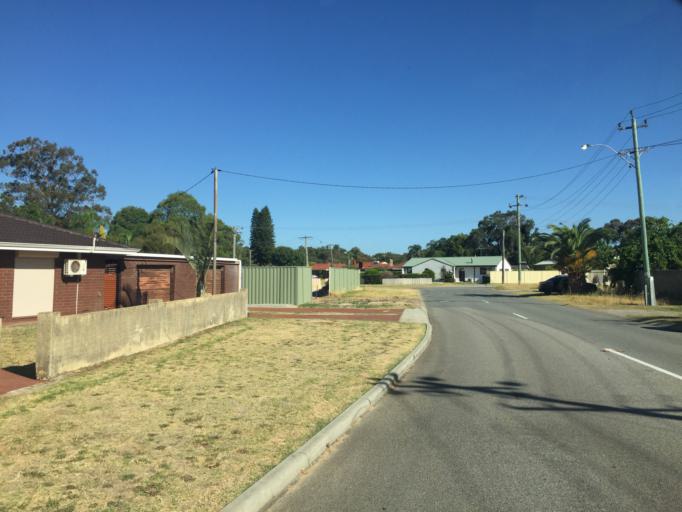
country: AU
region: Western Australia
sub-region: Canning
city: East Cannington
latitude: -32.0127
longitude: 115.9666
